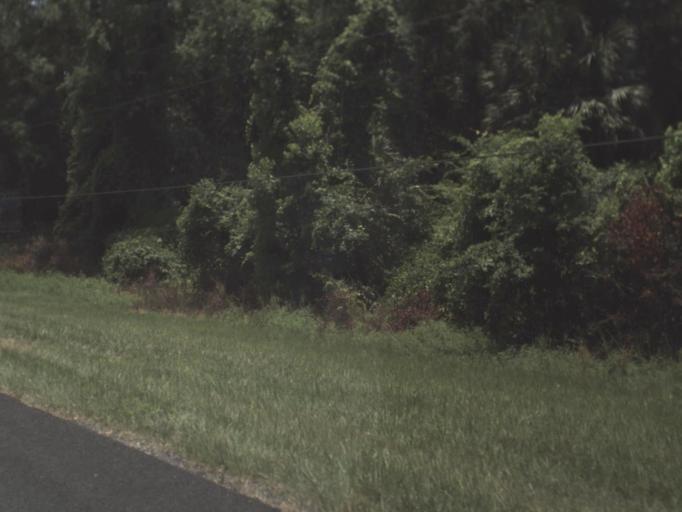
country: US
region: Florida
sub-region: Levy County
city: Manatee Road
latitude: 29.5874
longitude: -82.9596
